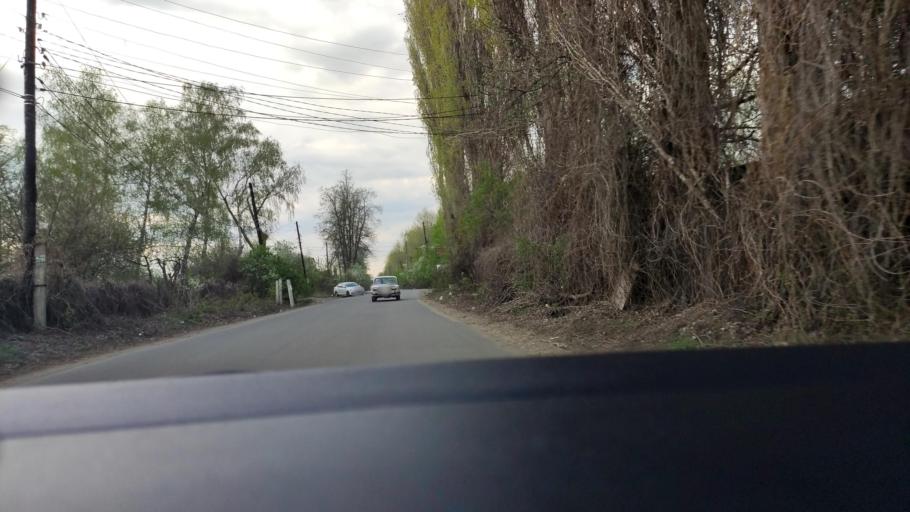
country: RU
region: Voronezj
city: Voronezh
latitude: 51.5988
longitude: 39.1676
